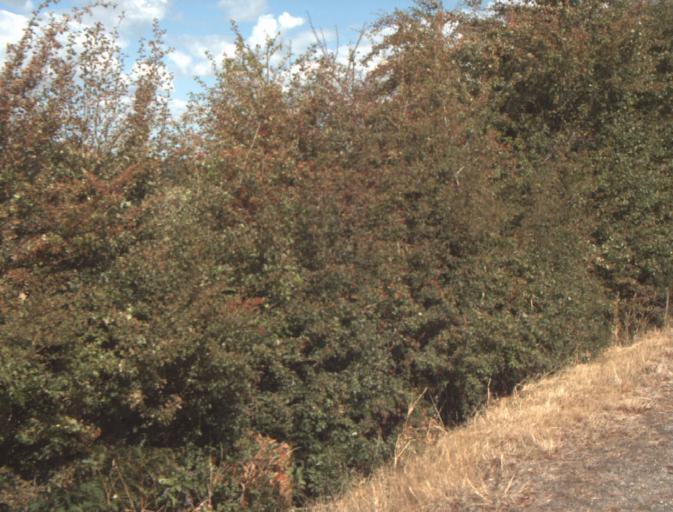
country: AU
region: Tasmania
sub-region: Launceston
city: Mayfield
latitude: -41.3126
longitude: 147.0446
